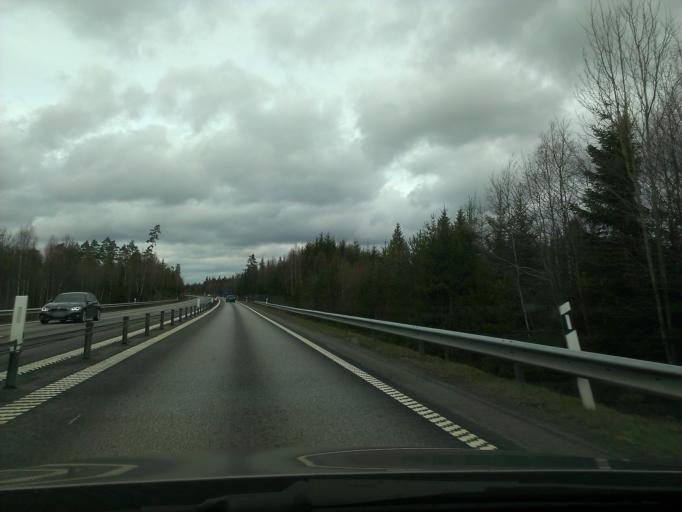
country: SE
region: Kronoberg
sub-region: Almhults Kommun
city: AElmhult
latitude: 56.4668
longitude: 14.1030
